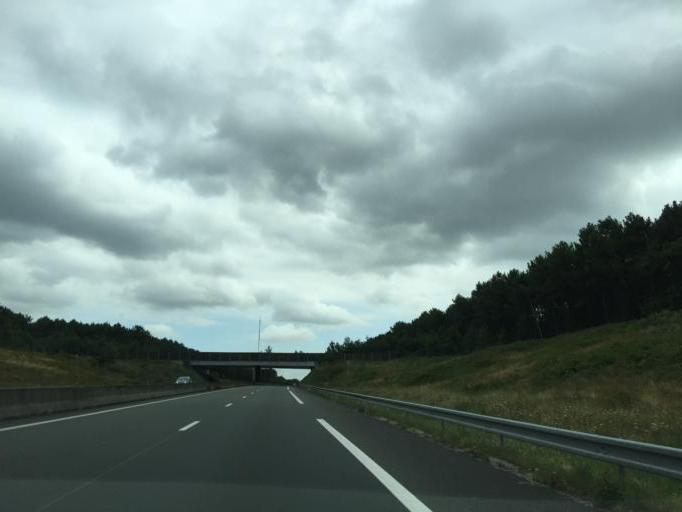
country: FR
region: Pays de la Loire
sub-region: Departement de la Sarthe
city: Mayet
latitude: 47.7861
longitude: 0.3077
